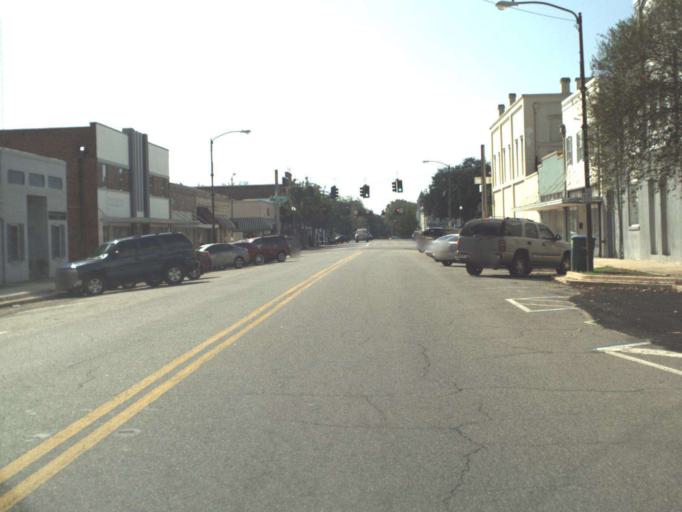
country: US
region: Florida
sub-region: Gadsden County
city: Quincy
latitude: 30.5901
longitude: -84.5758
